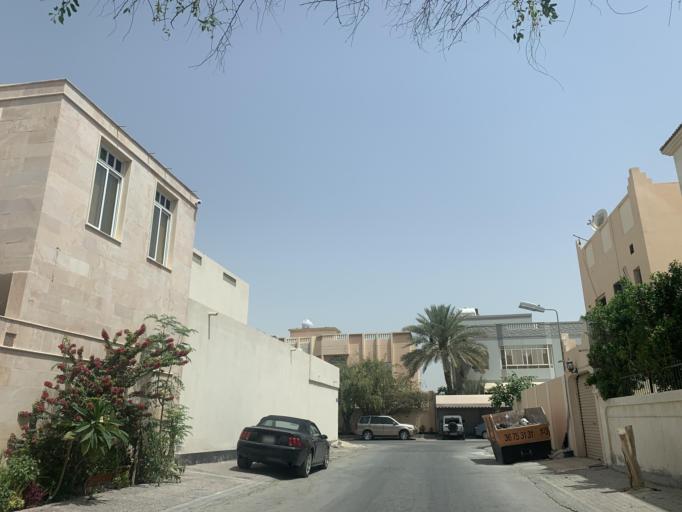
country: BH
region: Northern
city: Madinat `Isa
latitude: 26.1487
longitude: 50.5274
